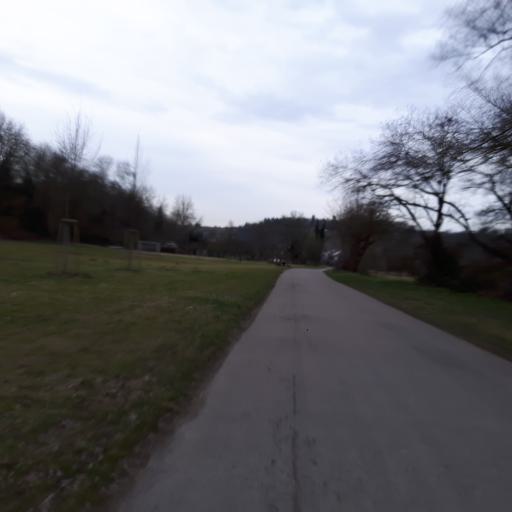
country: DE
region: Baden-Wuerttemberg
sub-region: Regierungsbezirk Stuttgart
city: Benningen am Neckar
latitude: 48.9433
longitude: 9.2498
